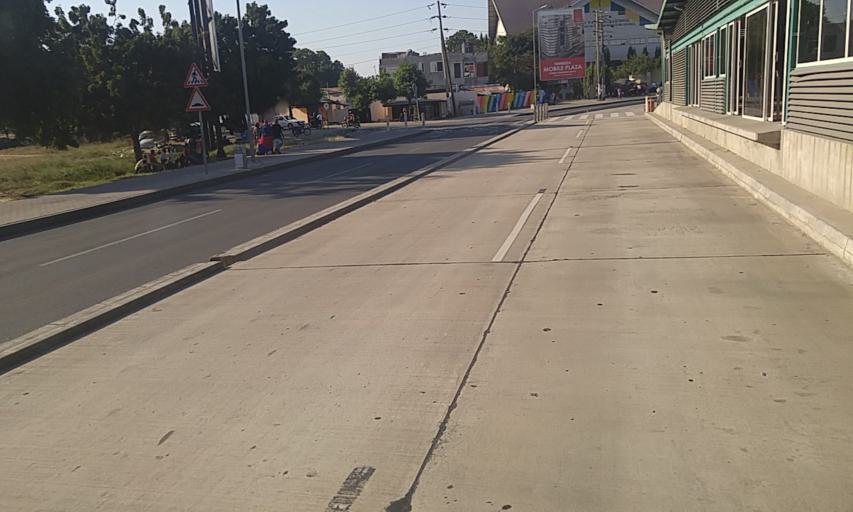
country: TZ
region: Dar es Salaam
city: Magomeni
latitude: -6.8056
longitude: 39.2585
